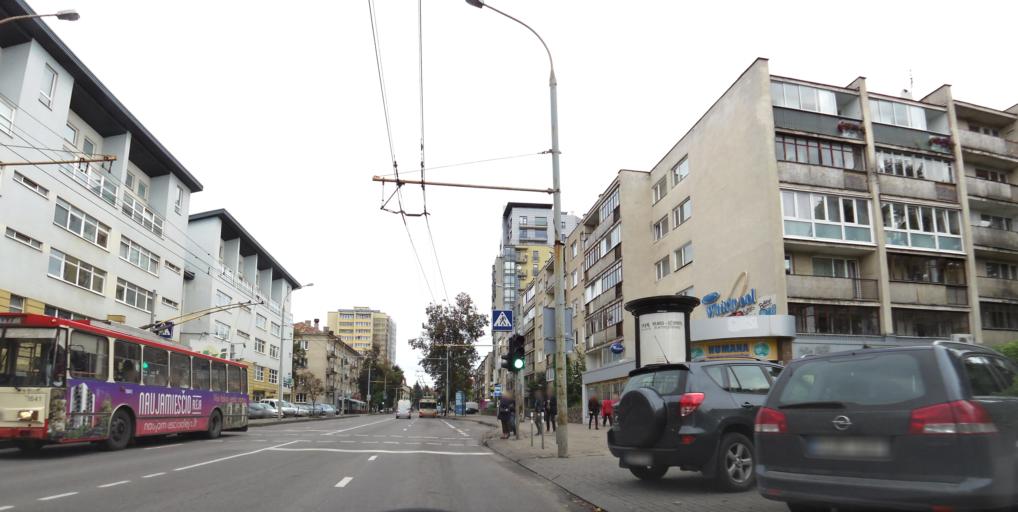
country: LT
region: Vilnius County
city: Rasos
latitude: 54.7027
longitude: 25.3098
